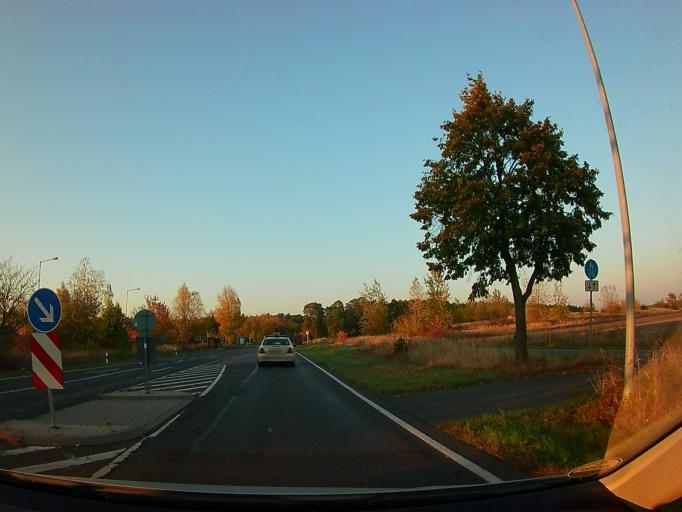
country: DE
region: Berlin
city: Bohnsdorf
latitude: 52.3763
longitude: 13.5658
